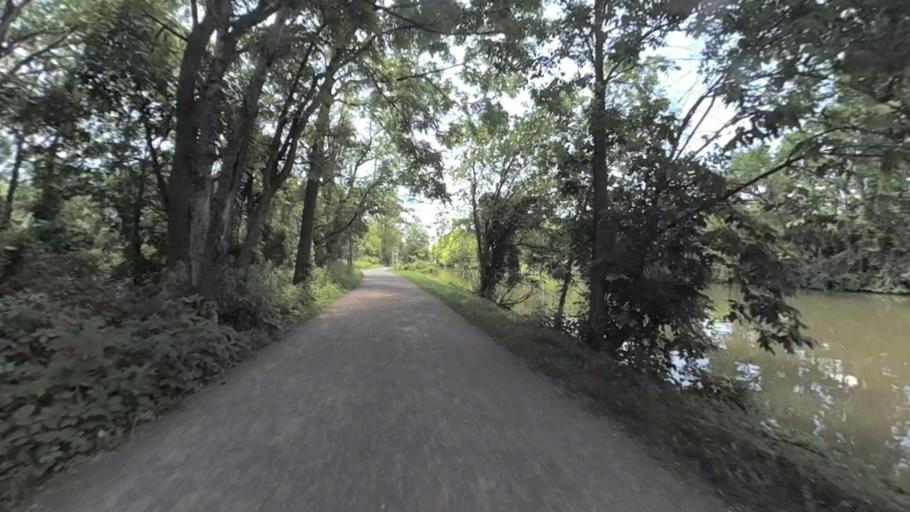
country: US
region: New York
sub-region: Monroe County
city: Pittsford
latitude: 43.0858
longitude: -77.5080
